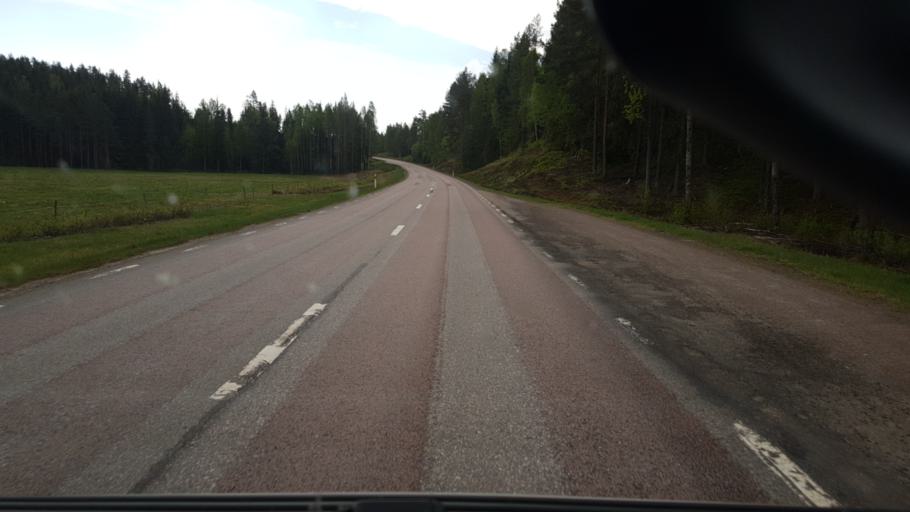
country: SE
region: Vaermland
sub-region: Arvika Kommun
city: Arvika
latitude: 59.5526
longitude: 12.7280
